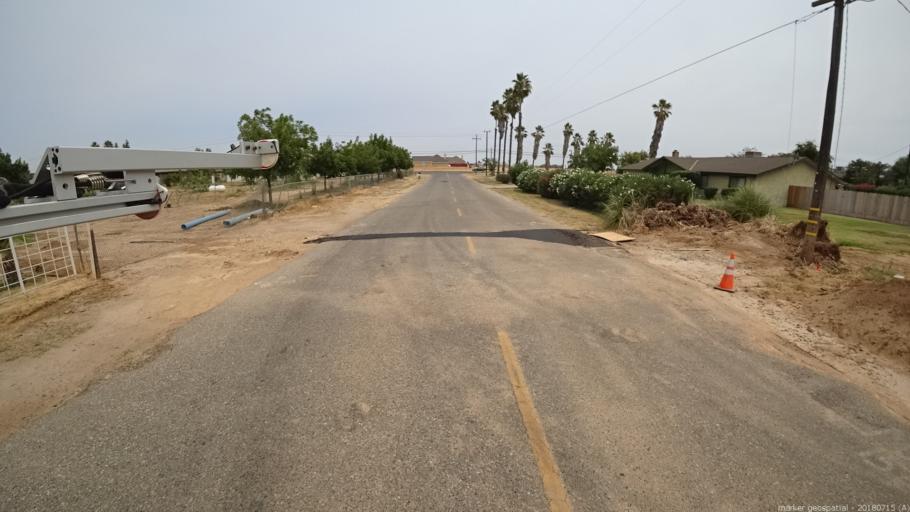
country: US
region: California
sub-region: Madera County
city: Madera Acres
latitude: 37.0141
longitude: -120.0757
